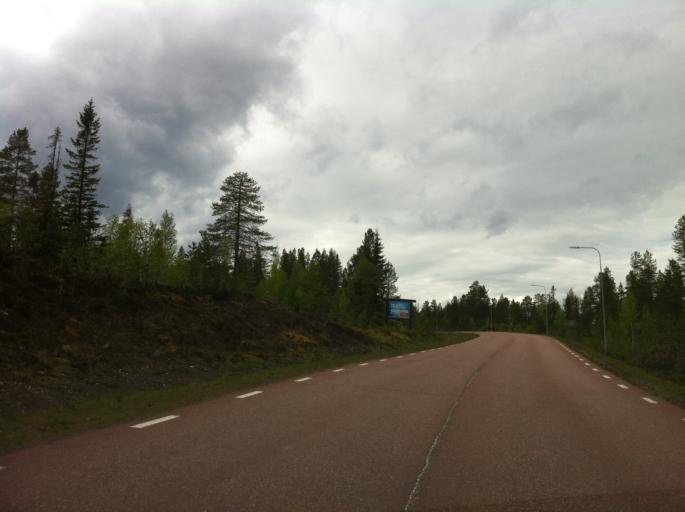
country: SE
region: Dalarna
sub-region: Malung-Saelens kommun
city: Malung
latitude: 61.1500
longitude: 13.2725
